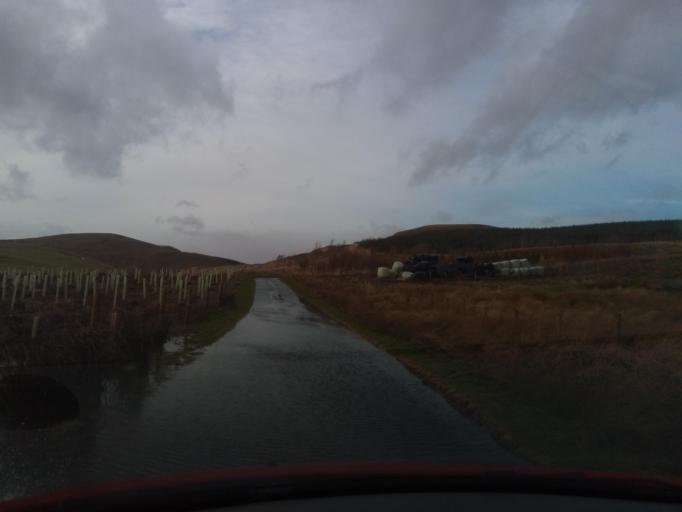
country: GB
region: Scotland
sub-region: The Scottish Borders
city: Jedburgh
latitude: 55.4316
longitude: -2.4217
